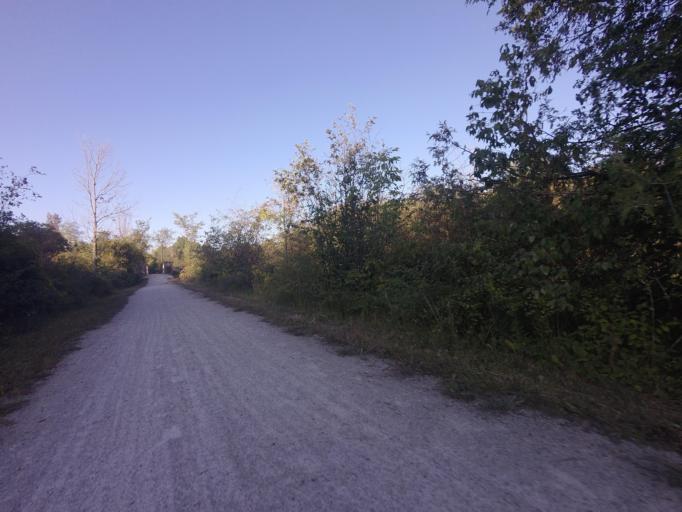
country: CA
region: Ontario
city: Orangeville
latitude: 43.8199
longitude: -79.9230
